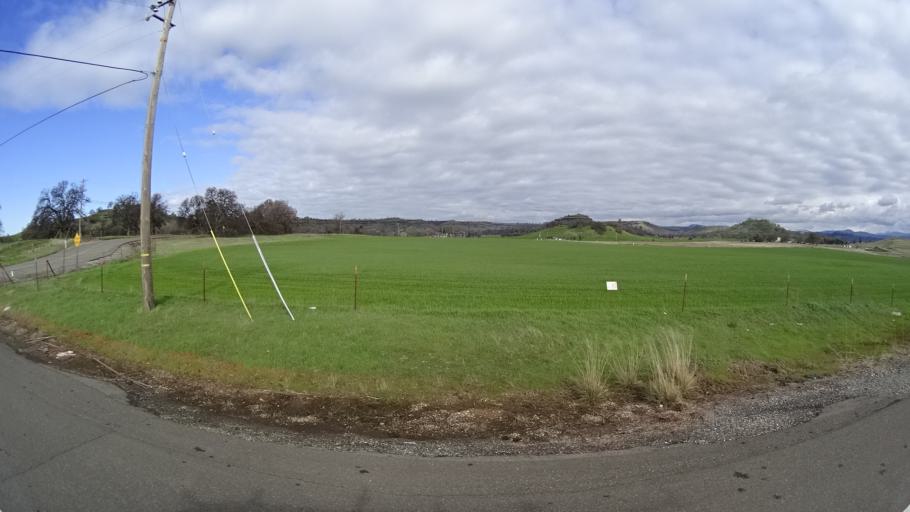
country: US
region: California
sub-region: Butte County
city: Paradise
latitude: 39.6403
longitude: -121.6595
